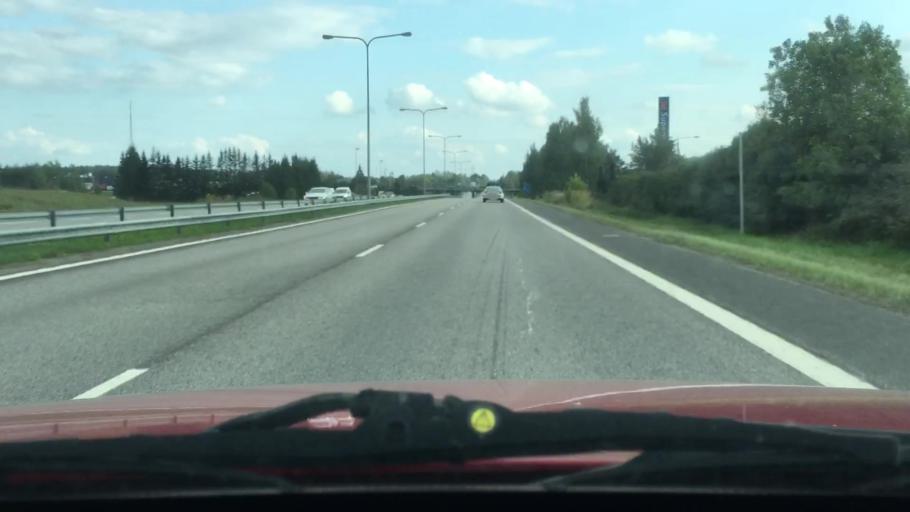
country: FI
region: Varsinais-Suomi
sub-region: Turku
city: Raisio
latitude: 60.4917
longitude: 22.1700
